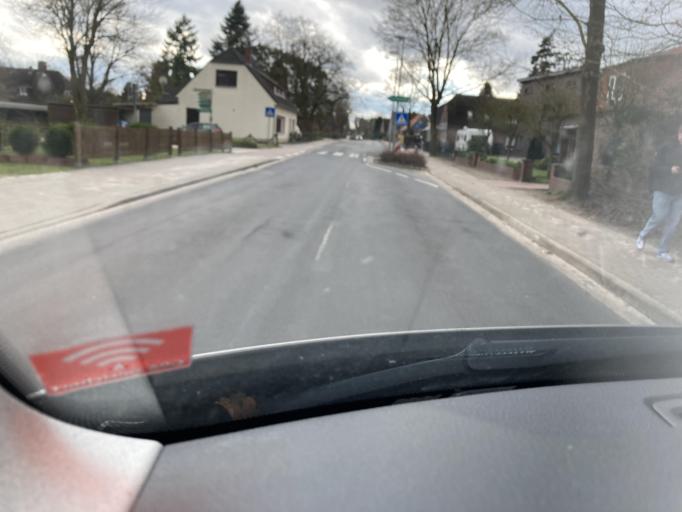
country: DE
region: Lower Saxony
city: Zetel
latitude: 53.4475
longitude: 7.9402
